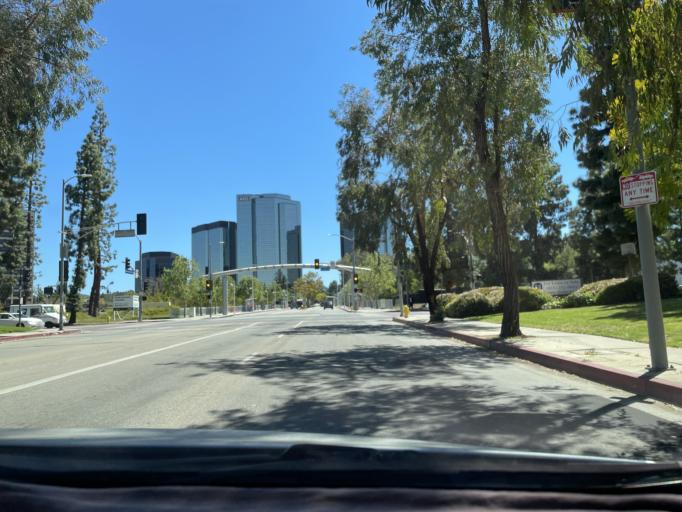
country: US
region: California
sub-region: Los Angeles County
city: Woodland Hills
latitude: 34.1834
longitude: -118.6015
